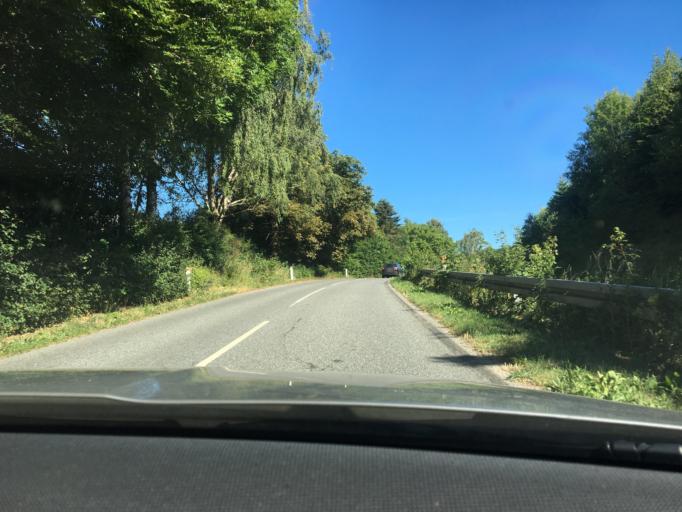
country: DK
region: Central Jutland
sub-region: Syddjurs Kommune
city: Hornslet
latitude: 56.3107
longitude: 10.3380
